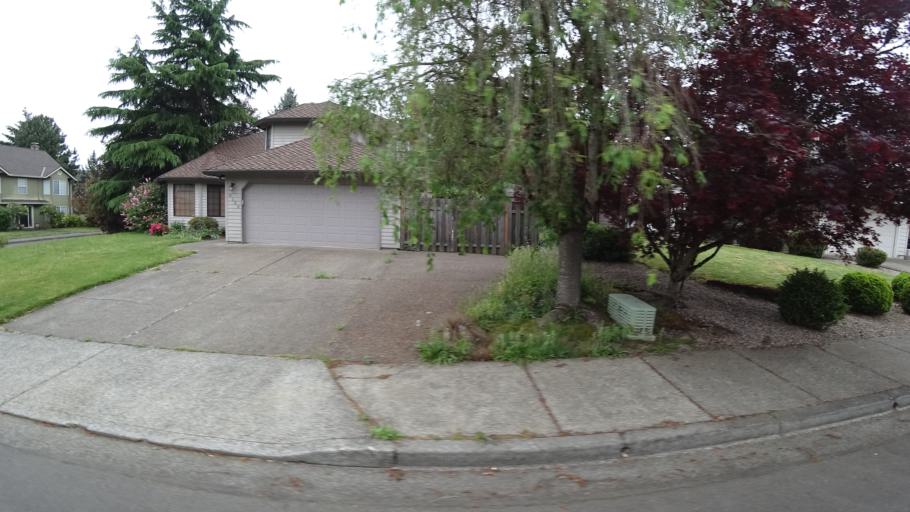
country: US
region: Oregon
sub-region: Washington County
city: Rockcreek
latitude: 45.5639
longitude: -122.8918
